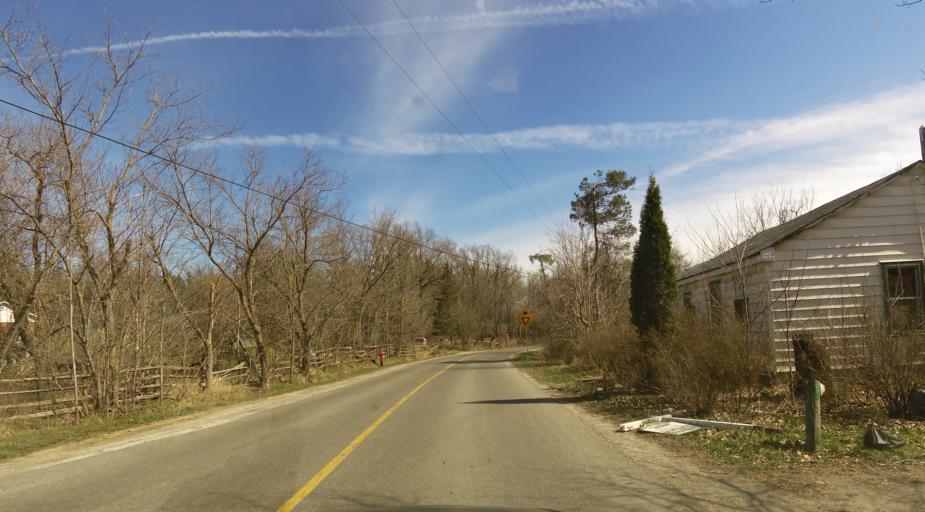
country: CA
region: Ontario
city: Brampton
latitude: 43.6440
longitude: -79.7708
